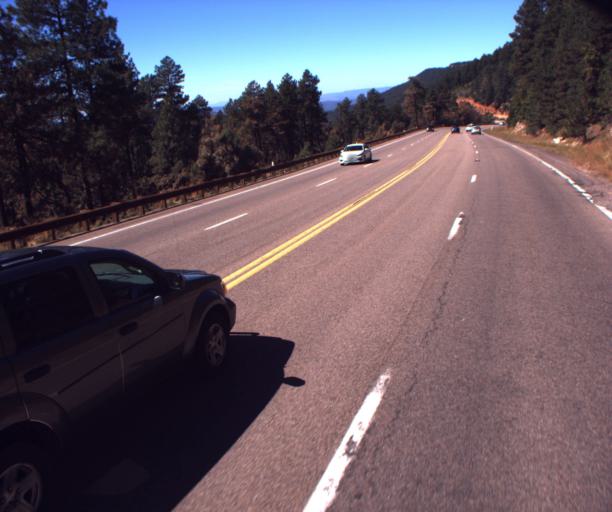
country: US
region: Arizona
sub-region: Gila County
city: Star Valley
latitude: 34.3012
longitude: -110.9093
